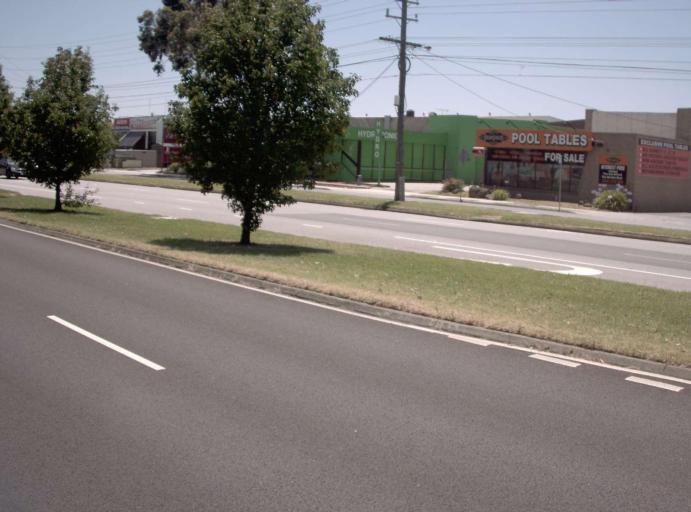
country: AU
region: Victoria
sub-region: Casey
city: Doveton
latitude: -38.0012
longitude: 145.2310
